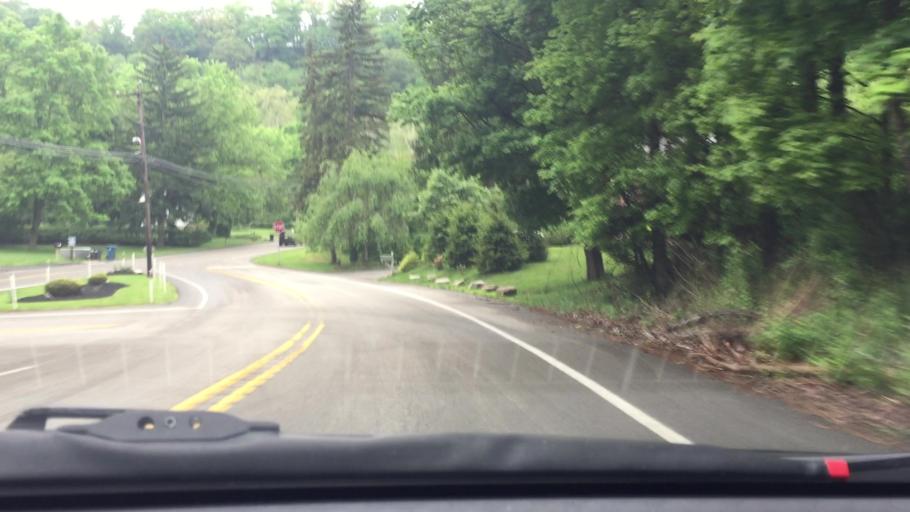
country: US
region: Pennsylvania
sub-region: Allegheny County
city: Glenshaw
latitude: 40.5320
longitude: -79.9601
